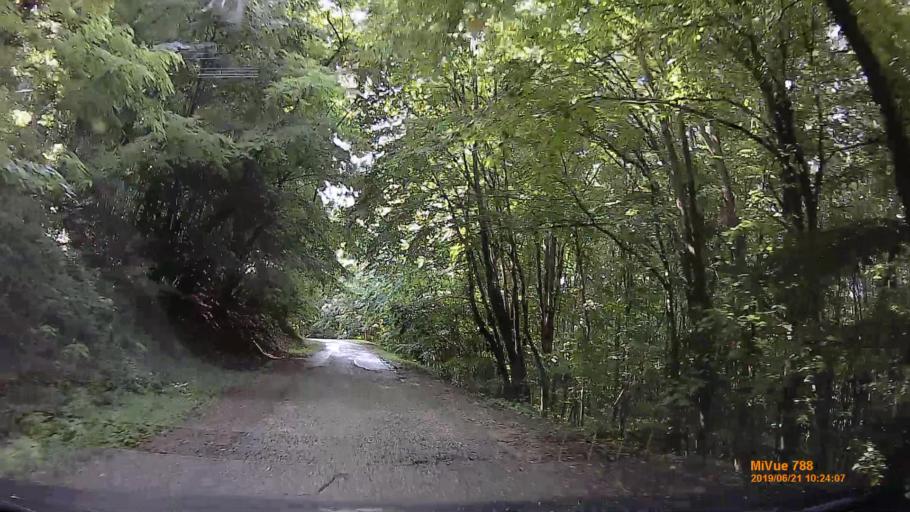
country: HU
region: Baranya
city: Buekkoesd
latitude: 46.1830
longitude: 17.9719
